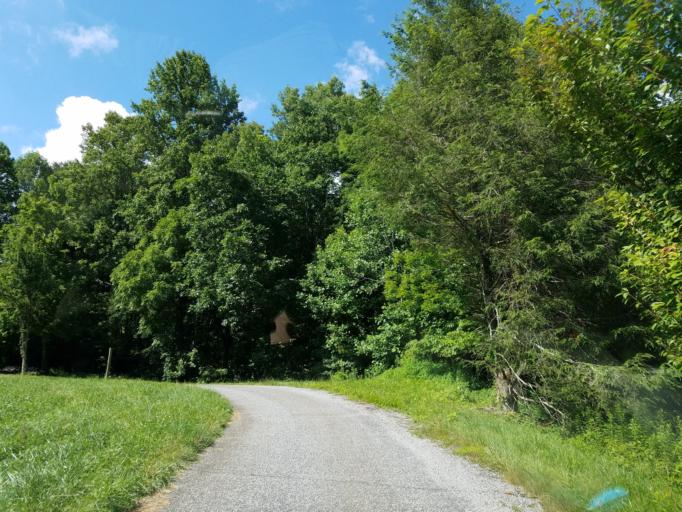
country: US
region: Georgia
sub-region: Lumpkin County
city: Dahlonega
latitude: 34.6681
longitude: -84.0355
